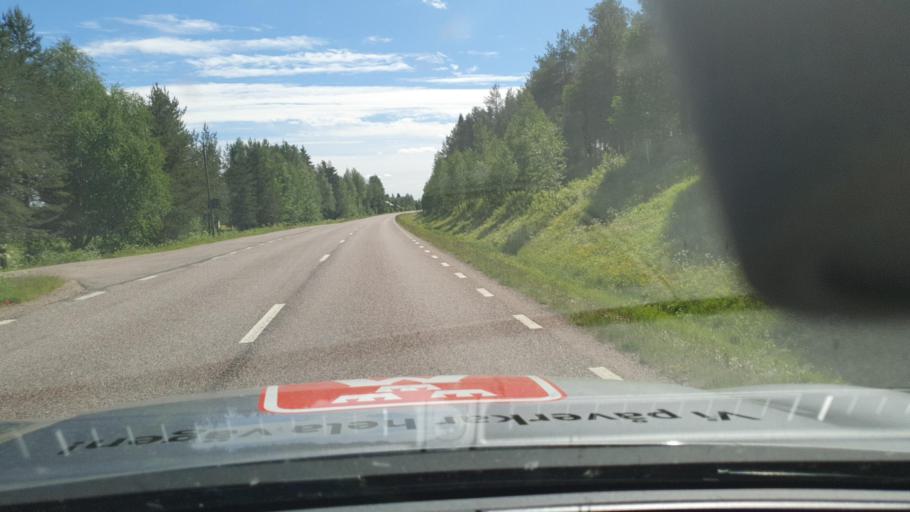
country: FI
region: Lapland
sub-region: Torniolaakso
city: Pello
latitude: 66.9501
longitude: 23.8475
